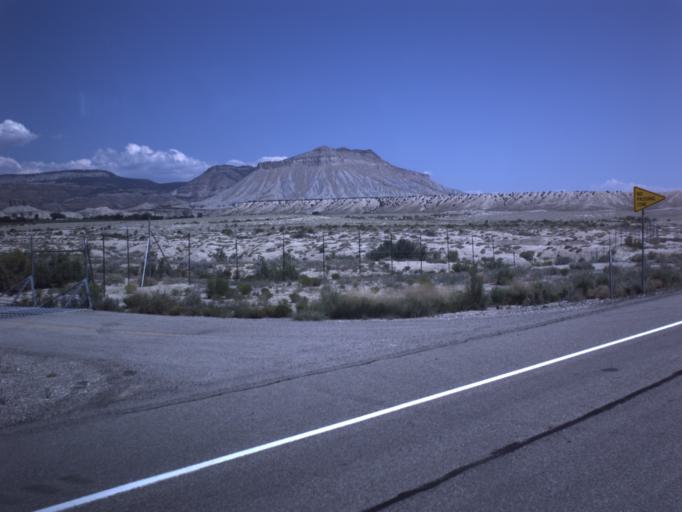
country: US
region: Utah
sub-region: Emery County
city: Ferron
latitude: 38.9393
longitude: -111.2232
